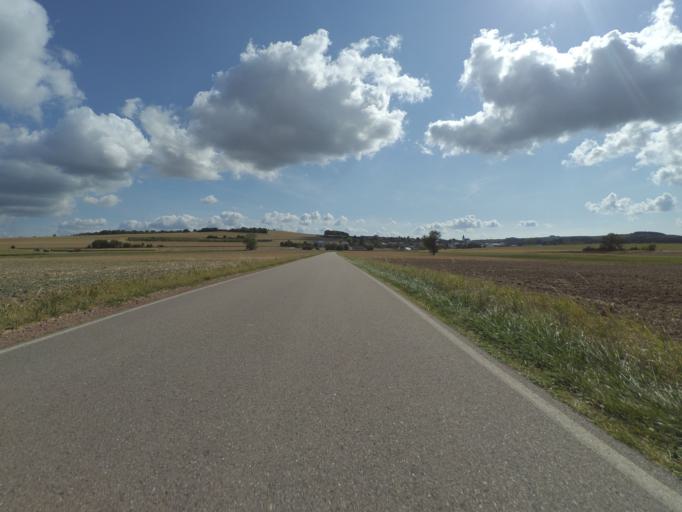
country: DE
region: Rheinland-Pfalz
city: Kirf
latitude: 49.5286
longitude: 6.4745
